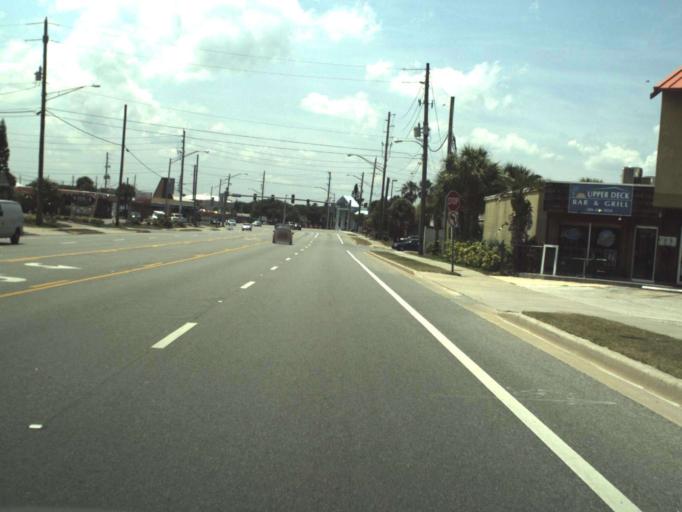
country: US
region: Florida
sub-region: Volusia County
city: New Smyrna Beach
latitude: 29.0277
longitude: -80.8910
